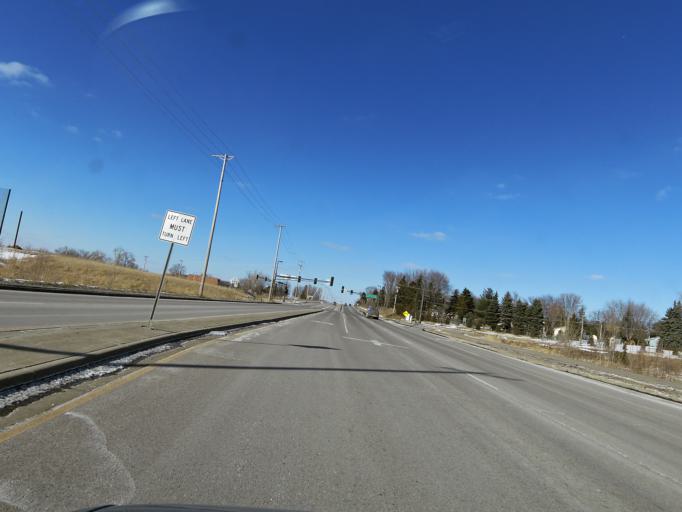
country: US
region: Minnesota
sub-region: Washington County
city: Woodbury
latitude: 44.9267
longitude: -92.9845
